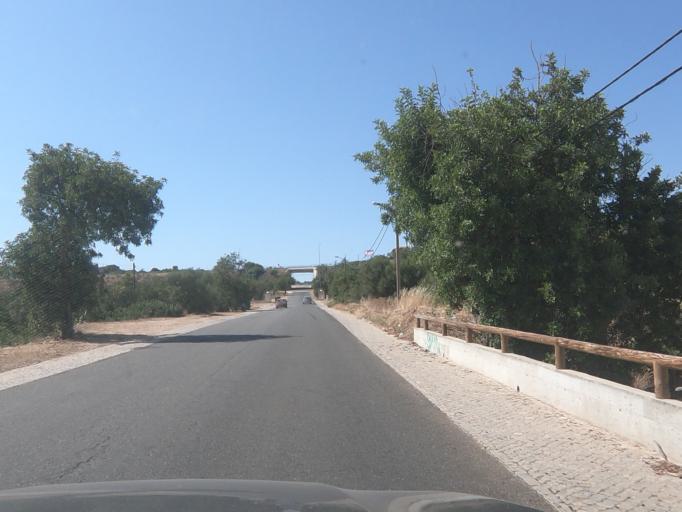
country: PT
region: Faro
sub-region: Faro
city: Santa Barbara de Nexe
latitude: 37.0903
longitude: -7.9938
